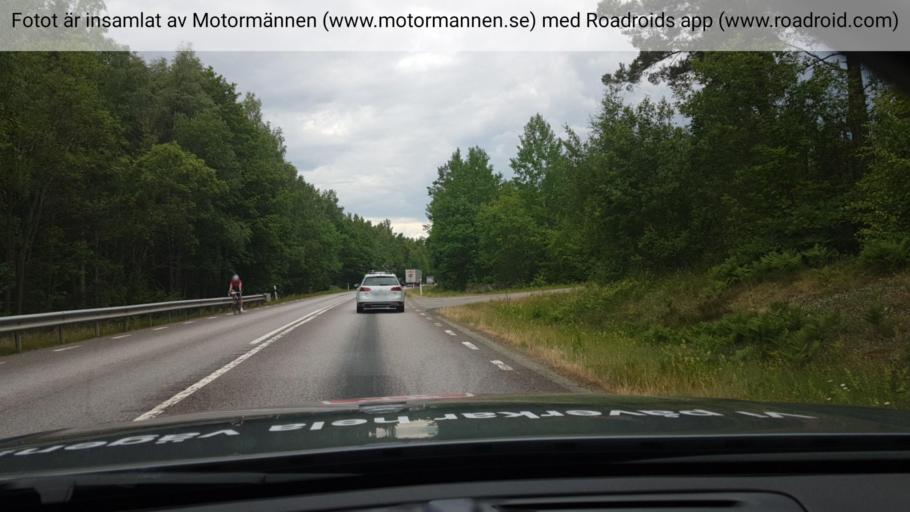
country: SE
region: OErebro
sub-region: Askersunds Kommun
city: Askersund
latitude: 58.7017
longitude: 14.7097
